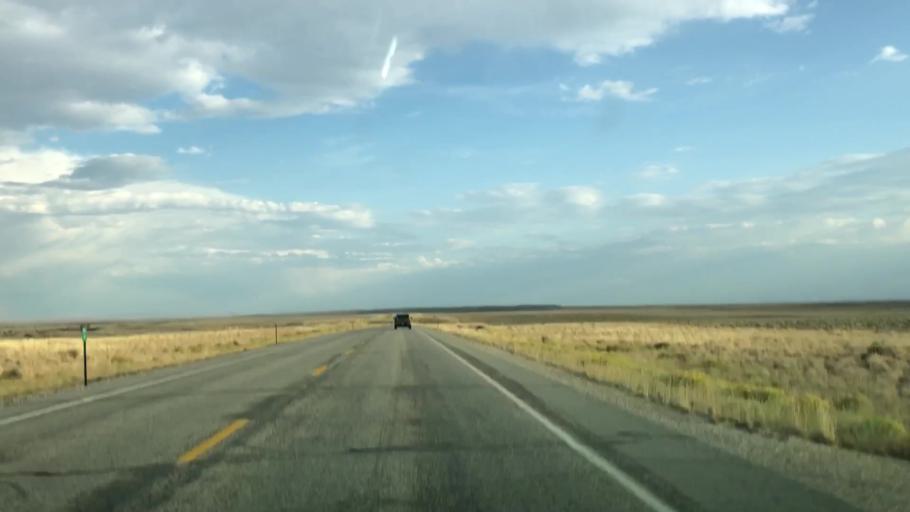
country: US
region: Wyoming
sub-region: Sublette County
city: Marbleton
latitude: 42.3336
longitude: -109.5180
